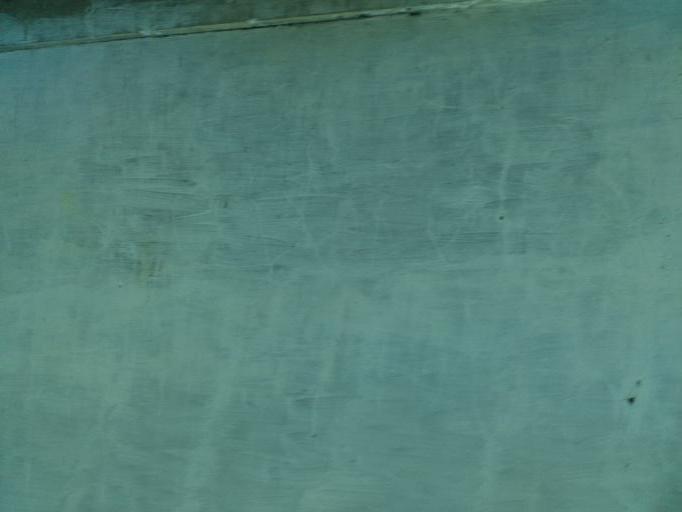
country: ID
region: Central Java
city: Delanggu
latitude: -7.6208
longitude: 110.7036
